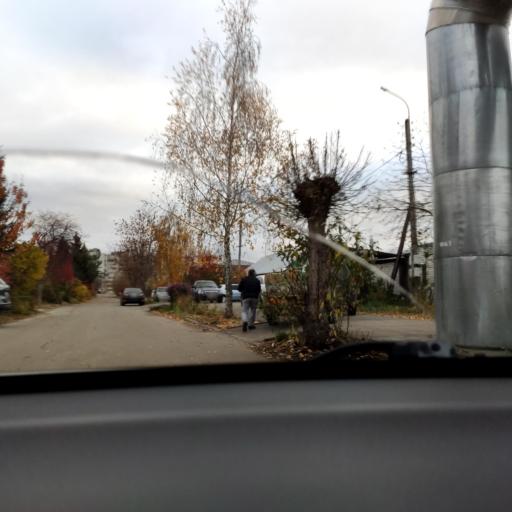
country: RU
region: Tatarstan
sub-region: Gorod Kazan'
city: Kazan
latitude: 55.8421
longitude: 49.1182
